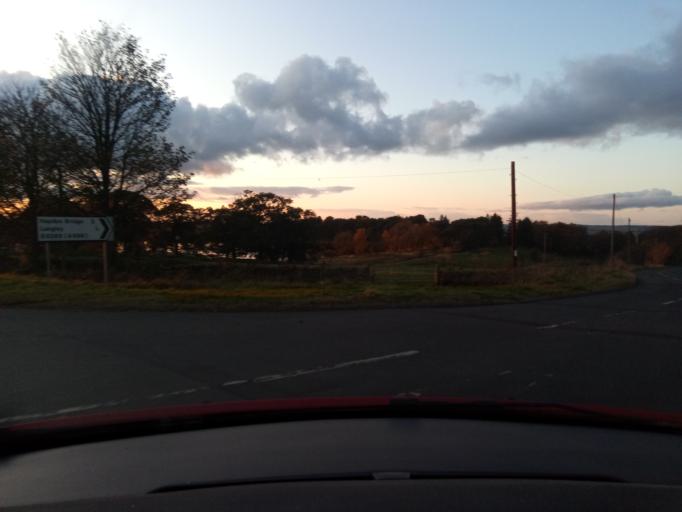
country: GB
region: England
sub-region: Northumberland
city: Bardon Mill
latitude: 54.9421
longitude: -2.2665
